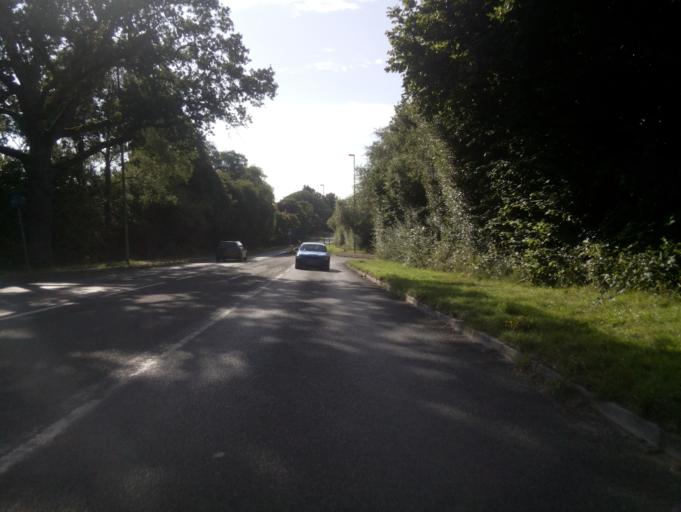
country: GB
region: England
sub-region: Hampshire
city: Romsey
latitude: 50.9816
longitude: -1.4459
